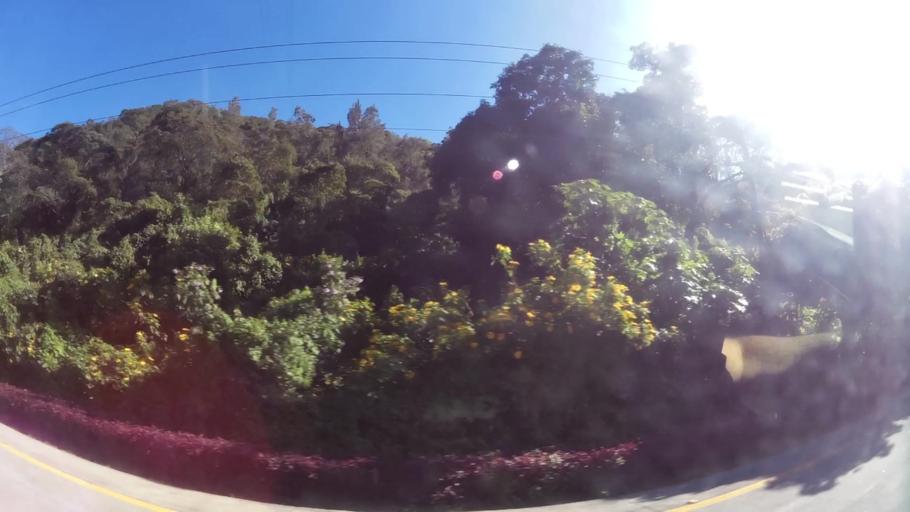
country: GT
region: Sacatepequez
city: Antigua Guatemala
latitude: 14.5597
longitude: -90.7116
